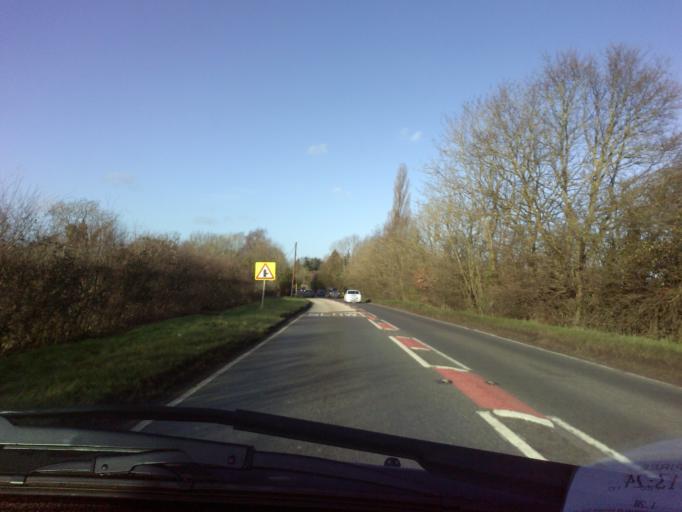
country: GB
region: England
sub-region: Hampshire
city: Romsey
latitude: 50.9672
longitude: -1.4773
